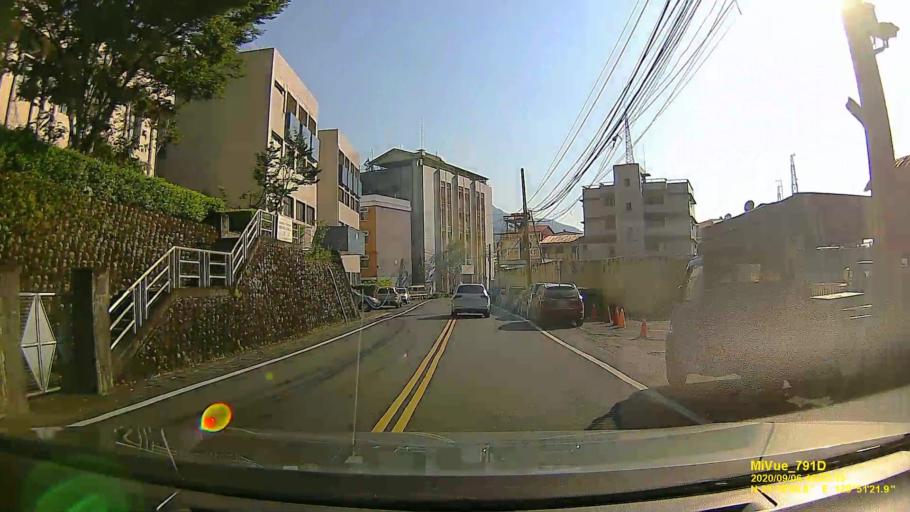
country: TW
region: Taiwan
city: Lugu
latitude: 23.8155
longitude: 120.8561
